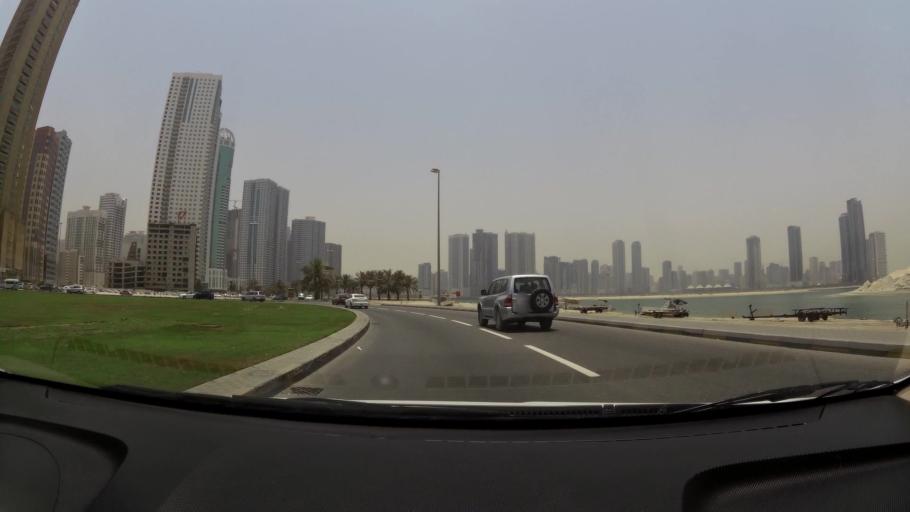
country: AE
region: Ash Shariqah
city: Sharjah
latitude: 25.3276
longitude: 55.3669
